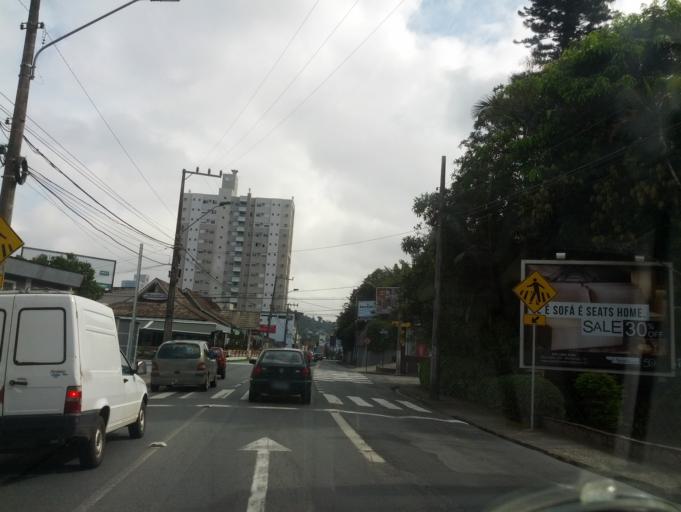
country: BR
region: Santa Catarina
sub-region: Blumenau
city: Blumenau
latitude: -26.9067
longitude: -49.0736
